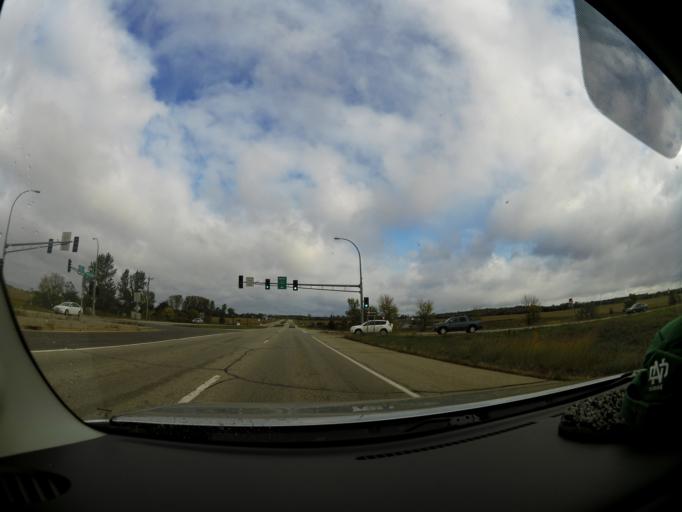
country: US
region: Minnesota
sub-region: Washington County
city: Lake Elmo
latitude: 44.9493
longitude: -92.8622
